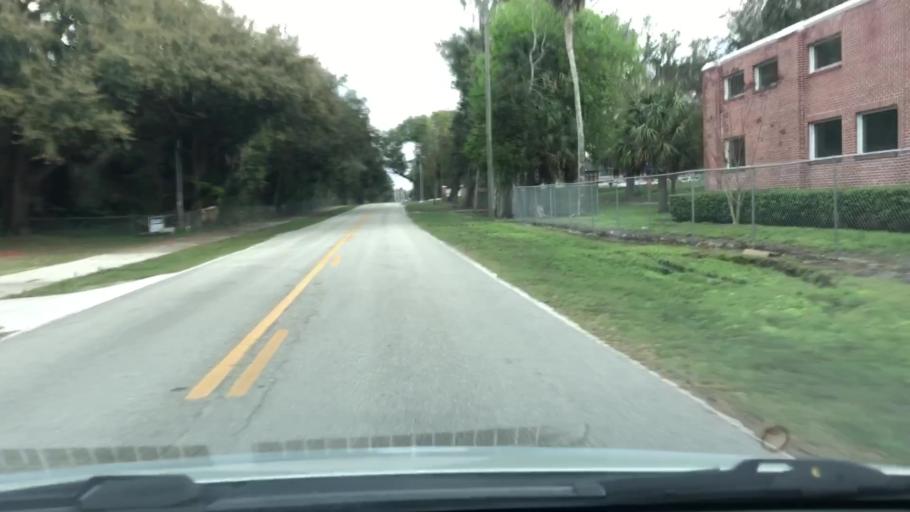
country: US
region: Florida
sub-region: Volusia County
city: Deltona
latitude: 28.8694
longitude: -81.2635
